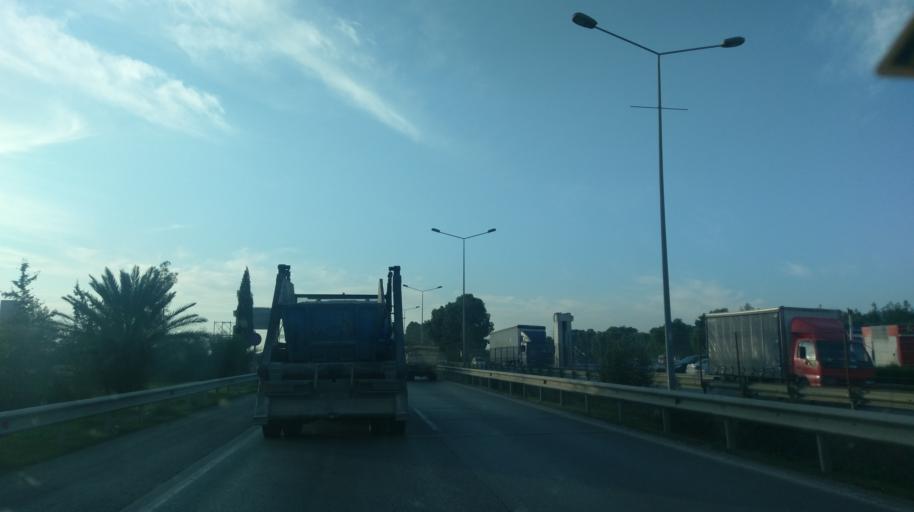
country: CY
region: Lefkosia
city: Nicosia
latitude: 35.2168
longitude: 33.4201
